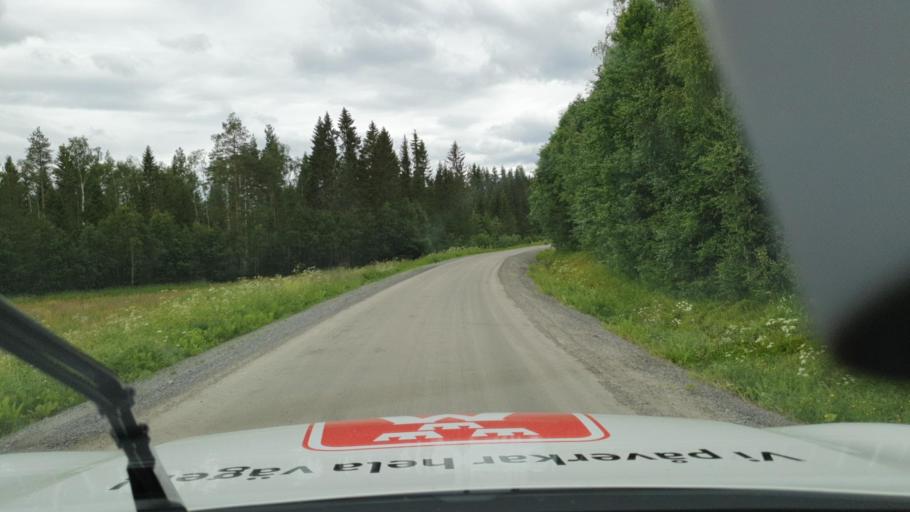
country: SE
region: Vaesterbotten
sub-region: Nordmalings Kommun
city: Nordmaling
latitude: 63.6888
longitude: 19.4447
